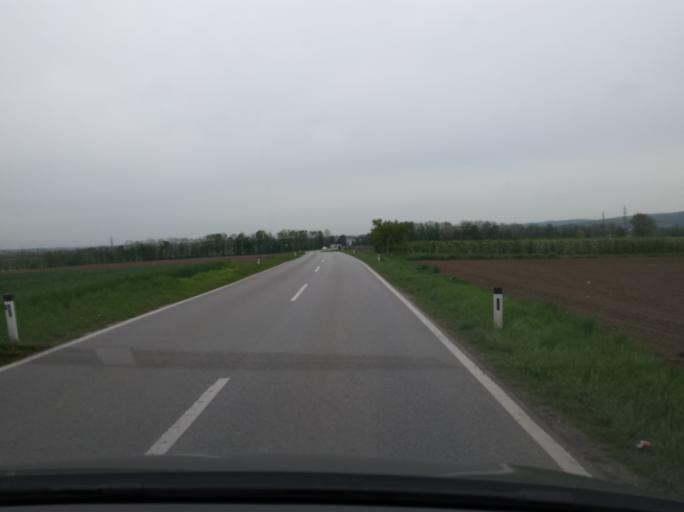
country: AT
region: Lower Austria
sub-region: Politischer Bezirk Bruck an der Leitha
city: Bruck an der Leitha
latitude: 48.0394
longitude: 16.7543
